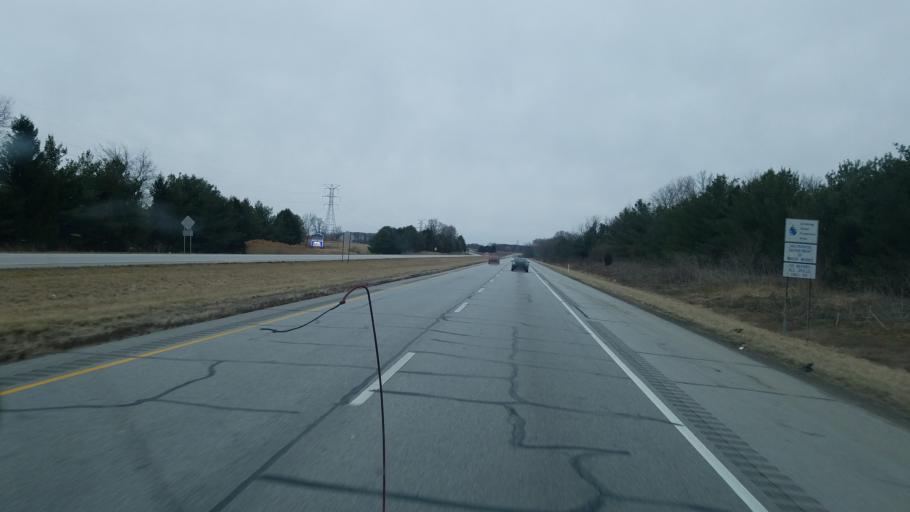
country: US
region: Indiana
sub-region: Porter County
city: Valparaiso
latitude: 41.5052
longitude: -87.0230
